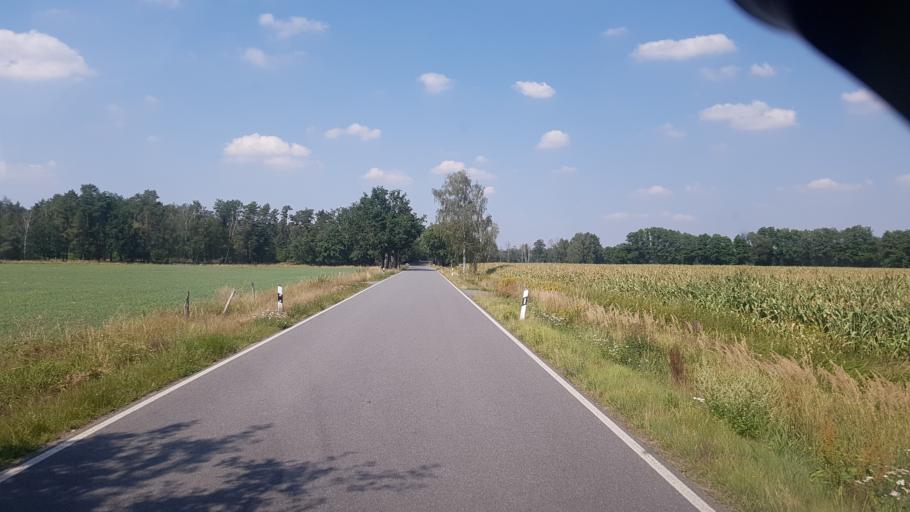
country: DE
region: Brandenburg
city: Cottbus
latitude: 51.7022
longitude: 14.4262
